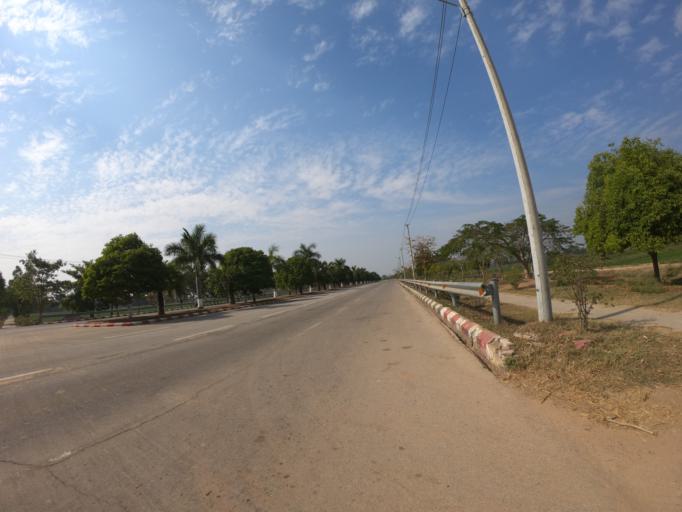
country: MM
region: Mandalay
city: Nay Pyi Taw
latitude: 19.6467
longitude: 96.1600
